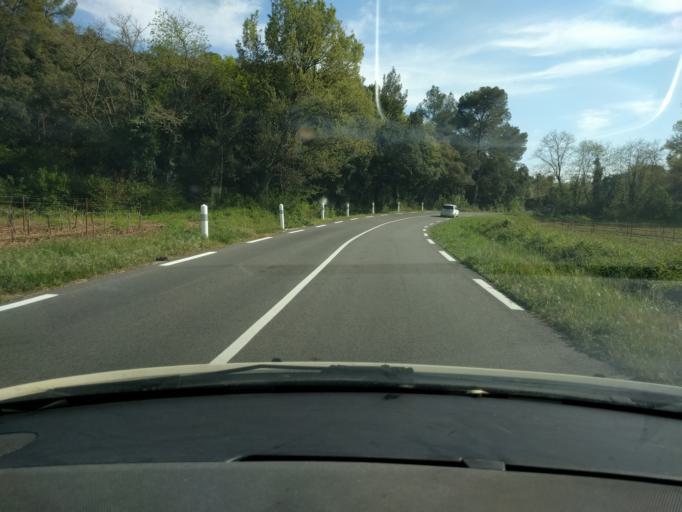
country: FR
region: Provence-Alpes-Cote d'Azur
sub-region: Departement du Var
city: Hyeres
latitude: 43.1554
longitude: 6.1288
